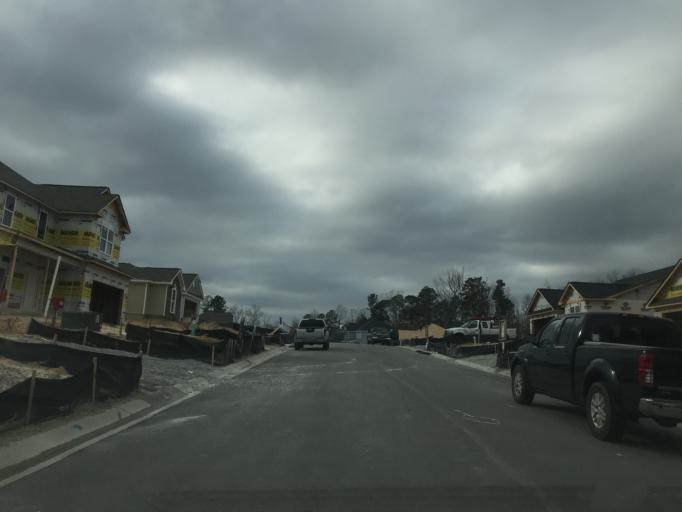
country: US
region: Georgia
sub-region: Columbia County
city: Grovetown
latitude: 33.4474
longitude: -82.1436
